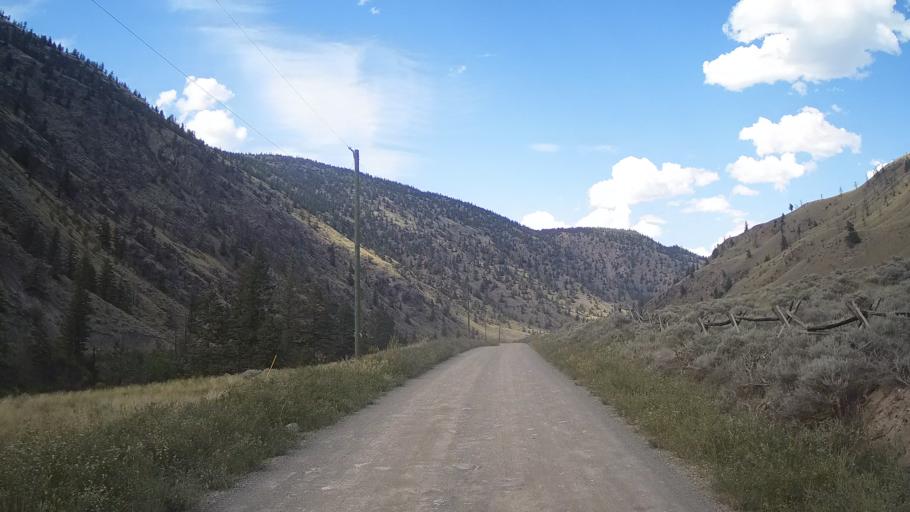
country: CA
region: British Columbia
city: Lillooet
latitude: 51.2048
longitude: -122.0985
